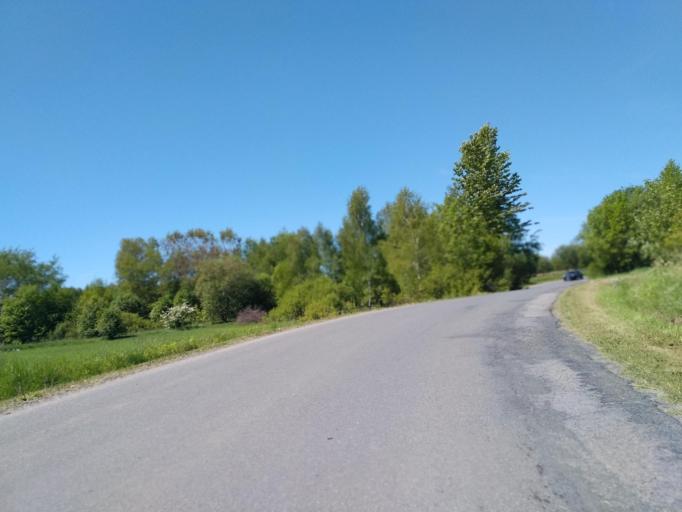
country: PL
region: Subcarpathian Voivodeship
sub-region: Powiat brzozowski
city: Gorki
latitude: 49.6572
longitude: 22.0301
